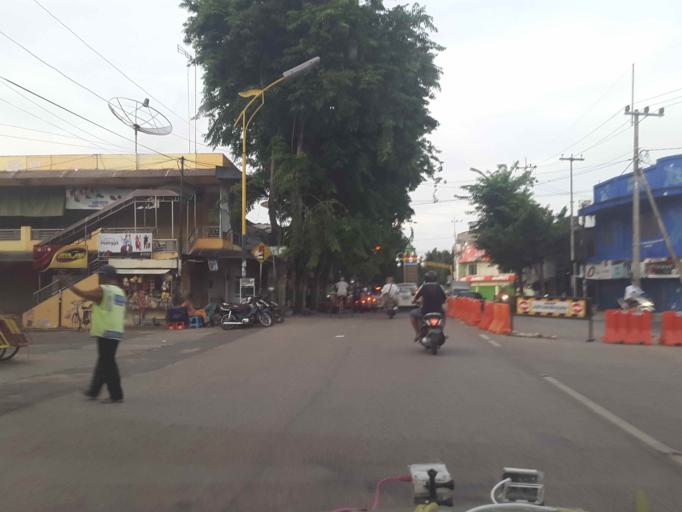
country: ID
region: East Java
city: Sumenep
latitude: -7.0077
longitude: 113.8597
